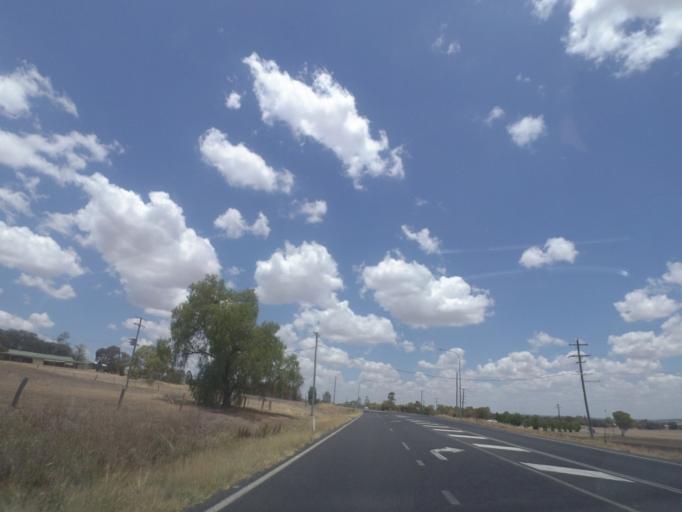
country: AU
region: Queensland
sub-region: Southern Downs
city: Warwick
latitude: -28.0231
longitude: 151.9852
